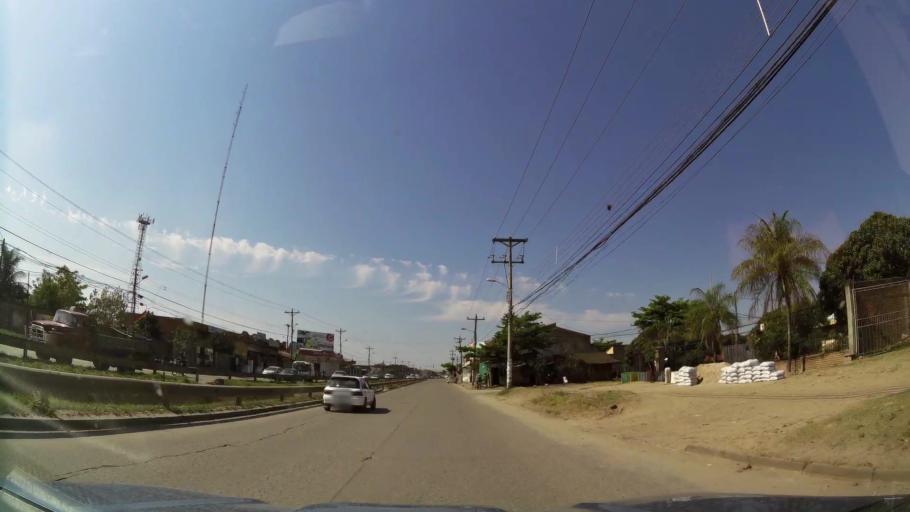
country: BO
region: Santa Cruz
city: Santa Cruz de la Sierra
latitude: -17.7484
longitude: -63.1242
